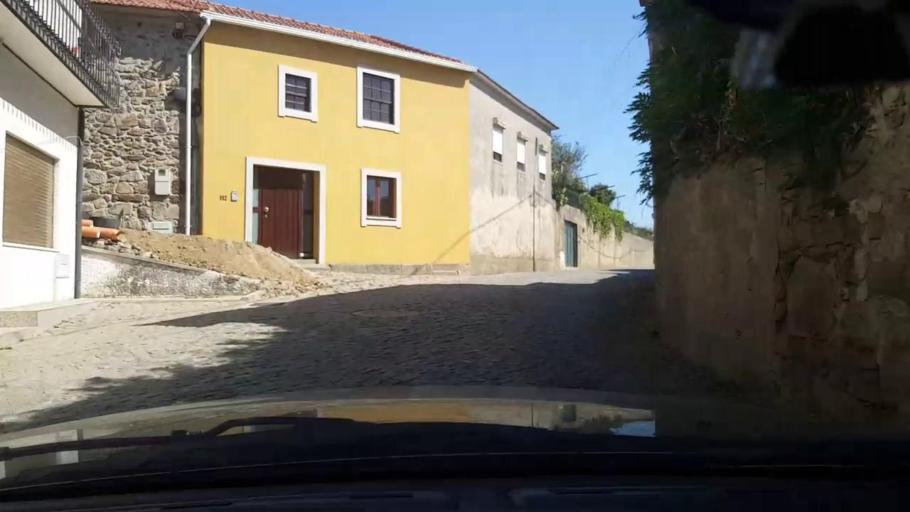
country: PT
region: Porto
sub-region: Matosinhos
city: Lavra
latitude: 41.2711
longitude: -8.6915
